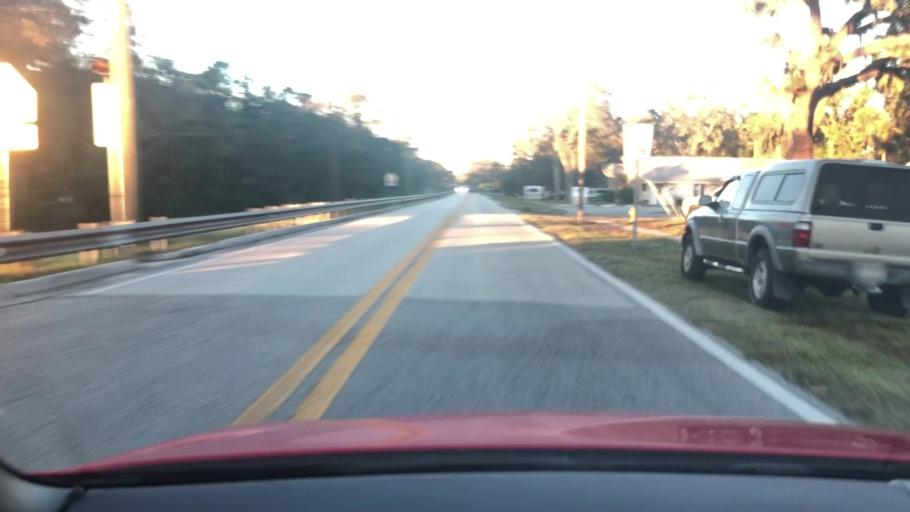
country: US
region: Florida
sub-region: Volusia County
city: South Daytona
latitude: 29.1586
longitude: -81.0032
